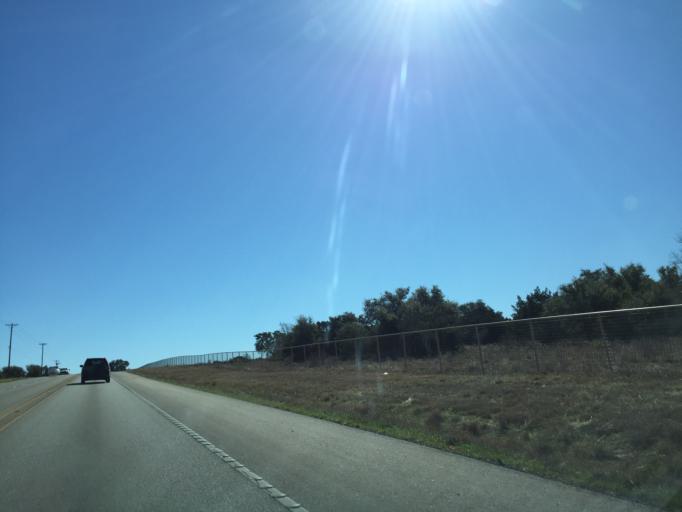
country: US
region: Texas
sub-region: Comal County
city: Canyon Lake
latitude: 29.7763
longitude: -98.3076
